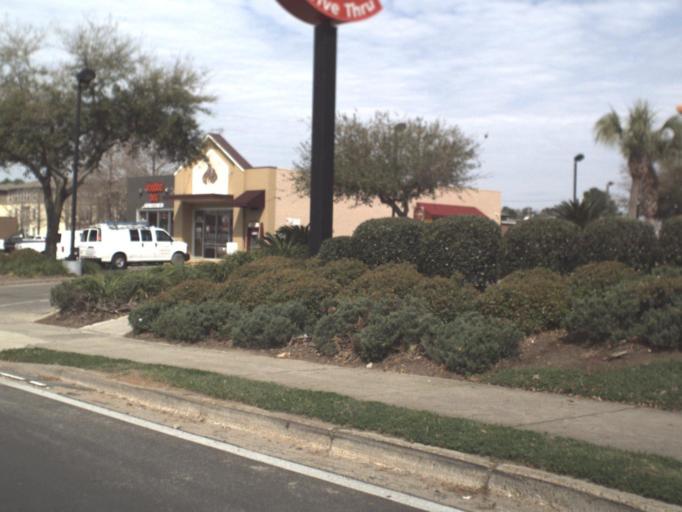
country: US
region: Florida
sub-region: Leon County
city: Tallahassee
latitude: 30.4491
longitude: -84.3052
